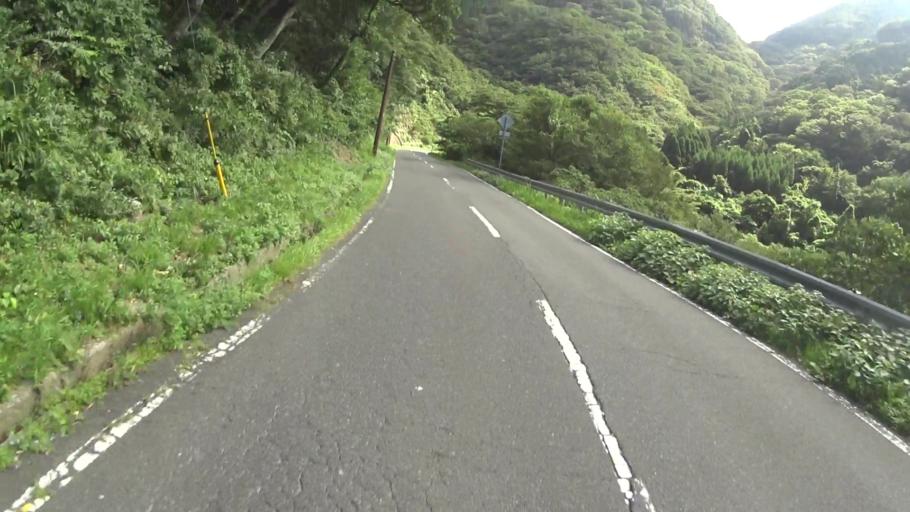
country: JP
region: Kyoto
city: Miyazu
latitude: 35.7690
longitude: 135.2263
